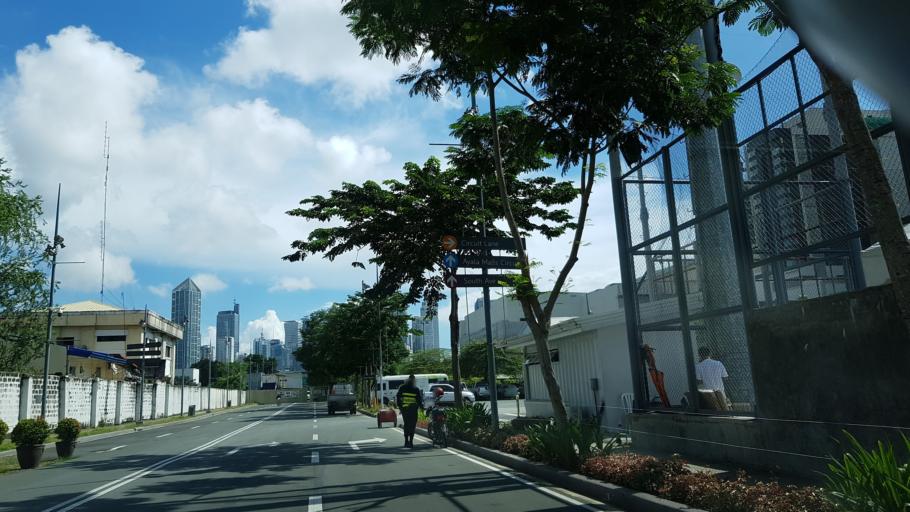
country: PH
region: Metro Manila
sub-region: Mandaluyong
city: Mandaluyong City
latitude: 14.5753
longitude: 121.0210
